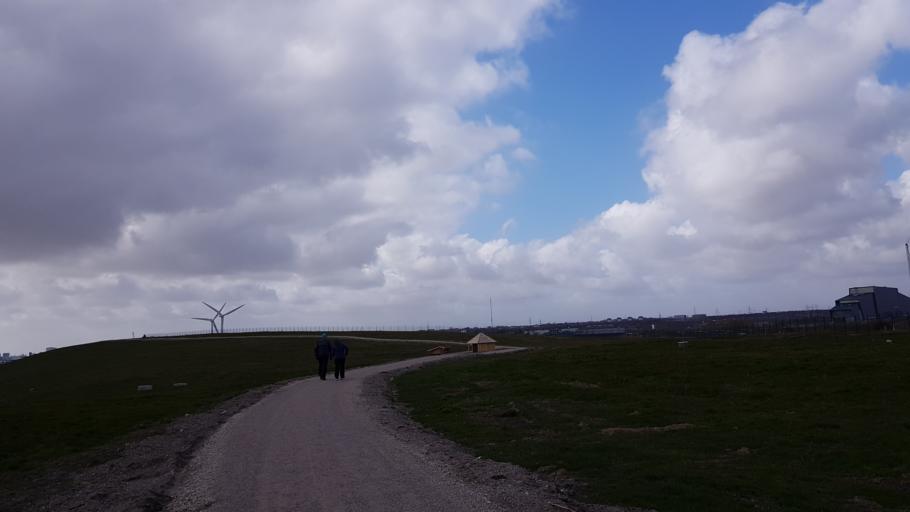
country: DK
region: South Denmark
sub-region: Esbjerg Kommune
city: Esbjerg
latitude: 55.4529
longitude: 8.5137
